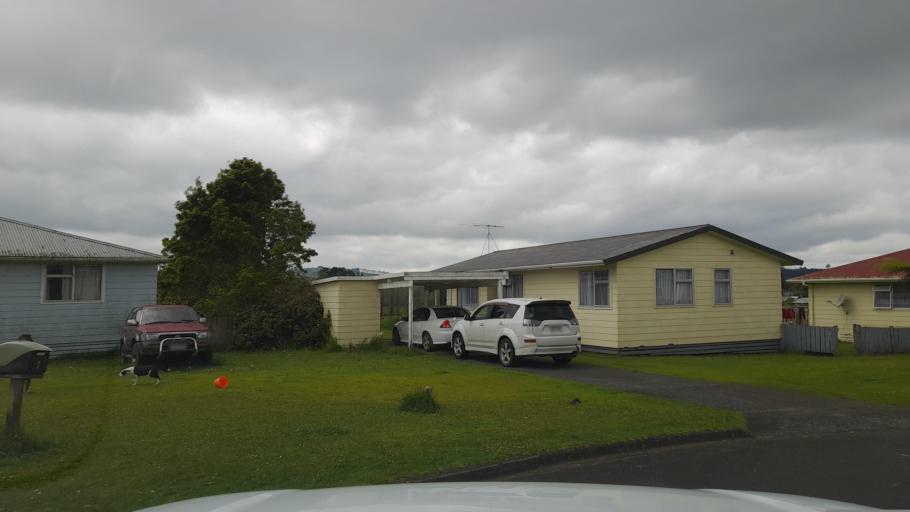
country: NZ
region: Northland
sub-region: Far North District
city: Waimate North
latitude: -35.4016
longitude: 173.7966
